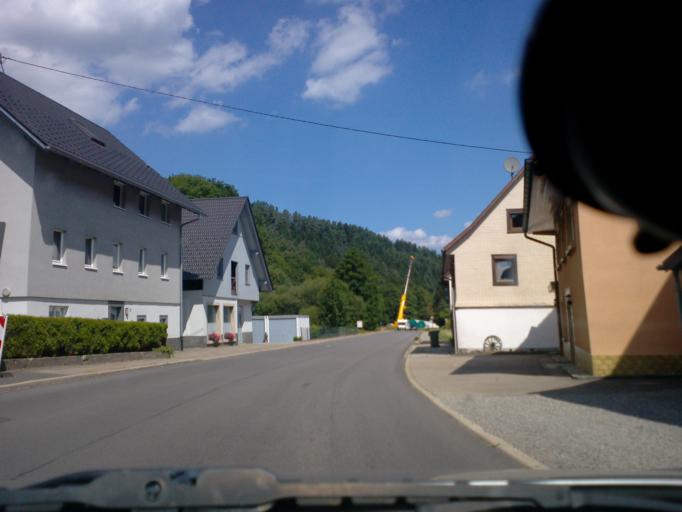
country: DE
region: Baden-Wuerttemberg
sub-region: Freiburg Region
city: Gutach (Schwarzwaldbahn)
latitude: 48.2344
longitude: 8.2147
